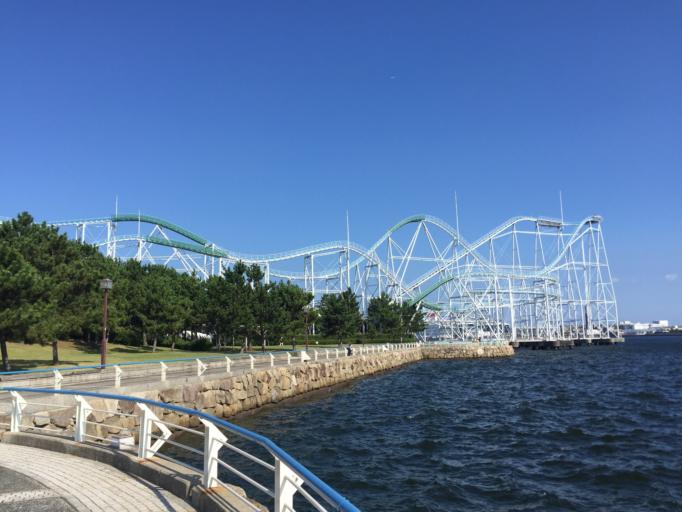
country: JP
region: Kanagawa
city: Yokosuka
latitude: 35.3353
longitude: 139.6420
